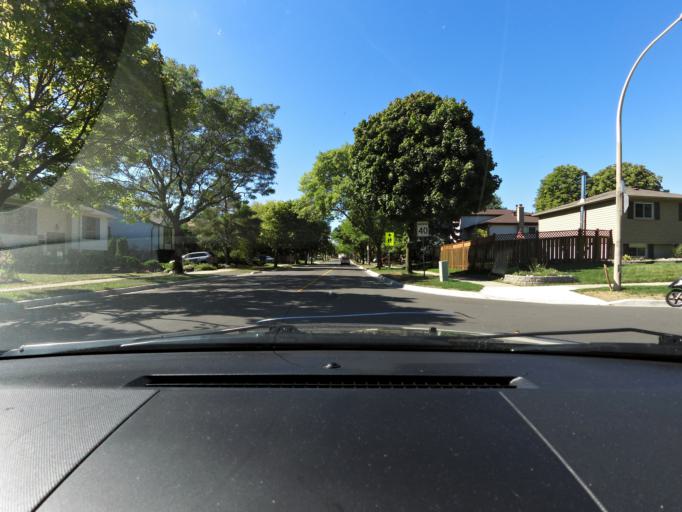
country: CA
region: Ontario
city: Burlington
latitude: 43.3701
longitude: -79.8101
